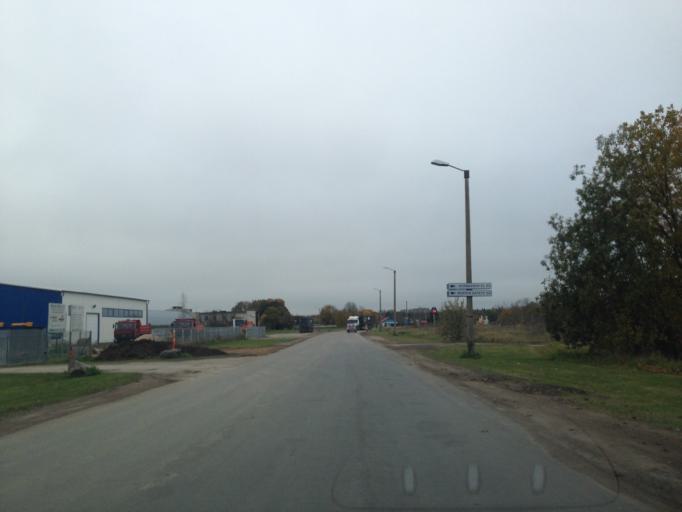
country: EE
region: Harju
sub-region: Harku vald
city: Tabasalu
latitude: 59.4236
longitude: 24.5412
